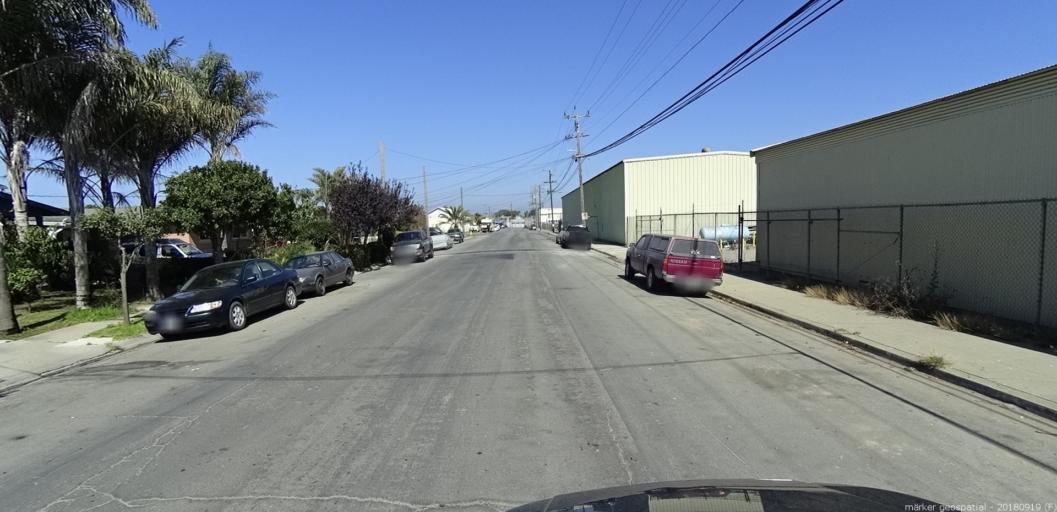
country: US
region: California
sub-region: Monterey County
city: Castroville
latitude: 36.7596
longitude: -121.7462
